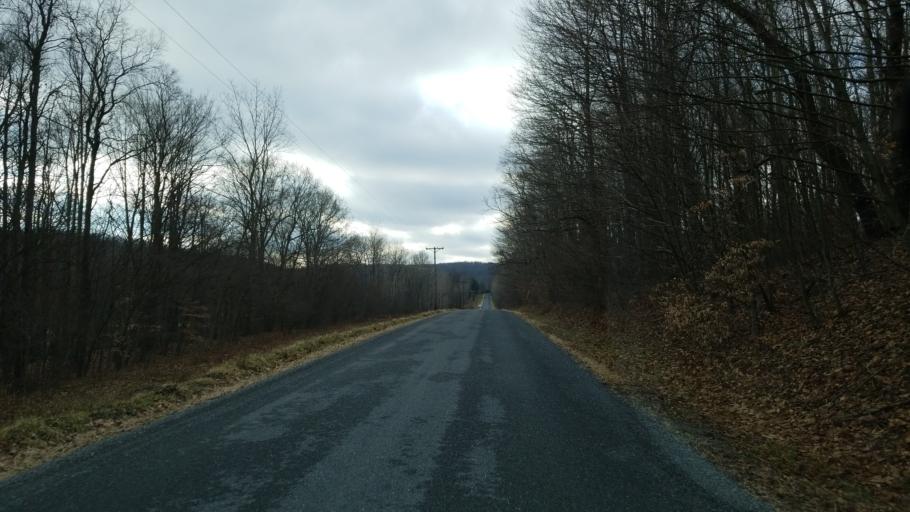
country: US
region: Pennsylvania
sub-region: Clearfield County
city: Treasure Lake
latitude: 41.1440
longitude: -78.5857
